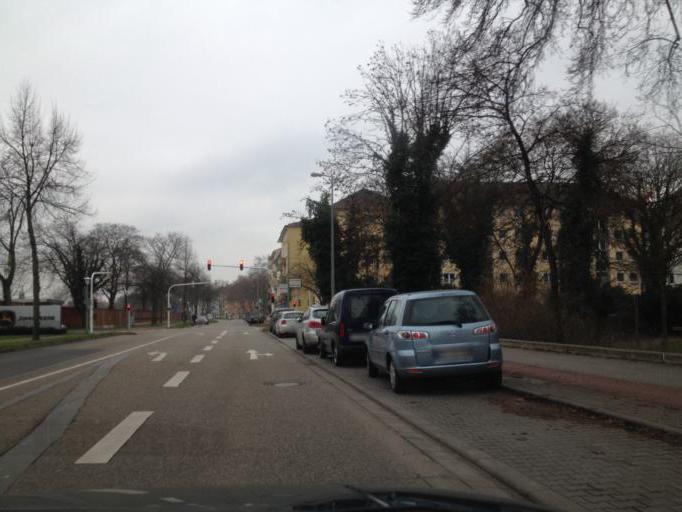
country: DE
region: Baden-Wuerttemberg
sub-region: Karlsruhe Region
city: Mannheim
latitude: 49.4712
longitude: 8.4717
